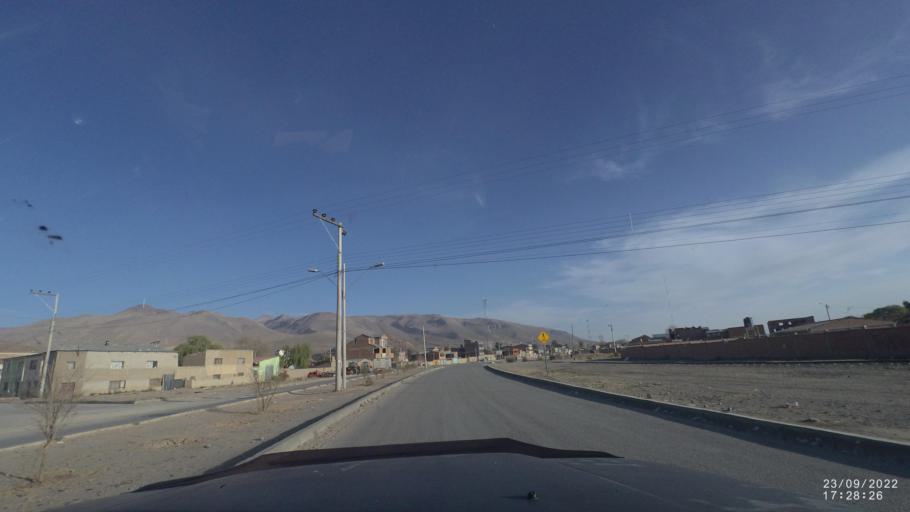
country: BO
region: Oruro
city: Challapata
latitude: -18.8956
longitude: -66.7772
